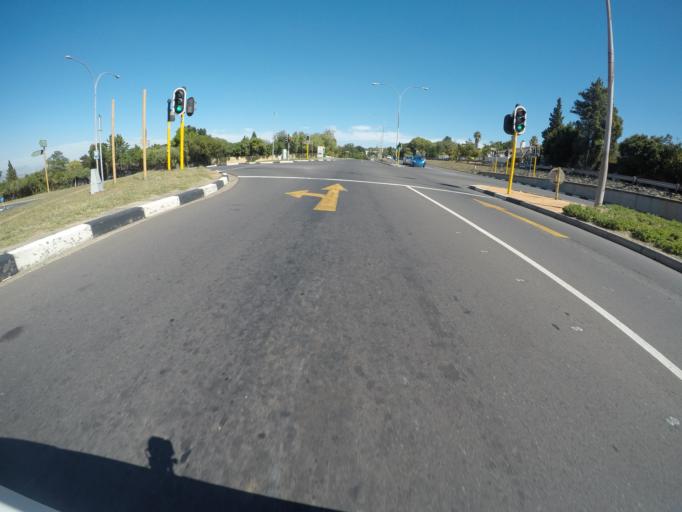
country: ZA
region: Western Cape
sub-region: City of Cape Town
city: Kraaifontein
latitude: -33.8424
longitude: 18.6474
